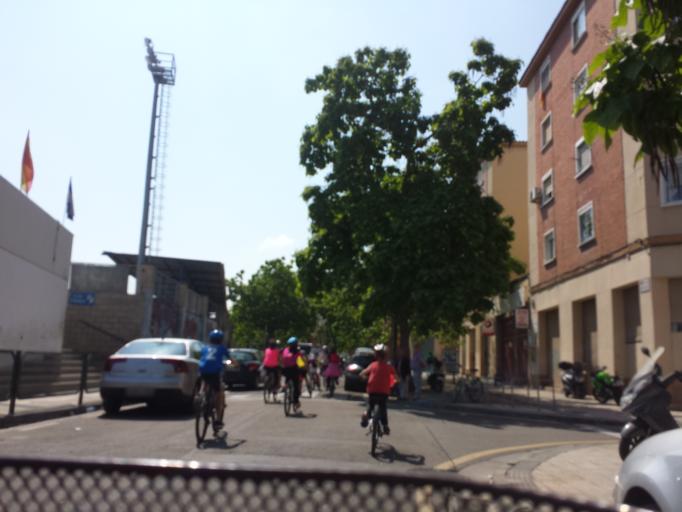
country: ES
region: Aragon
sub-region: Provincia de Zaragoza
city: Almozara
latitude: 41.6617
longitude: -0.8949
